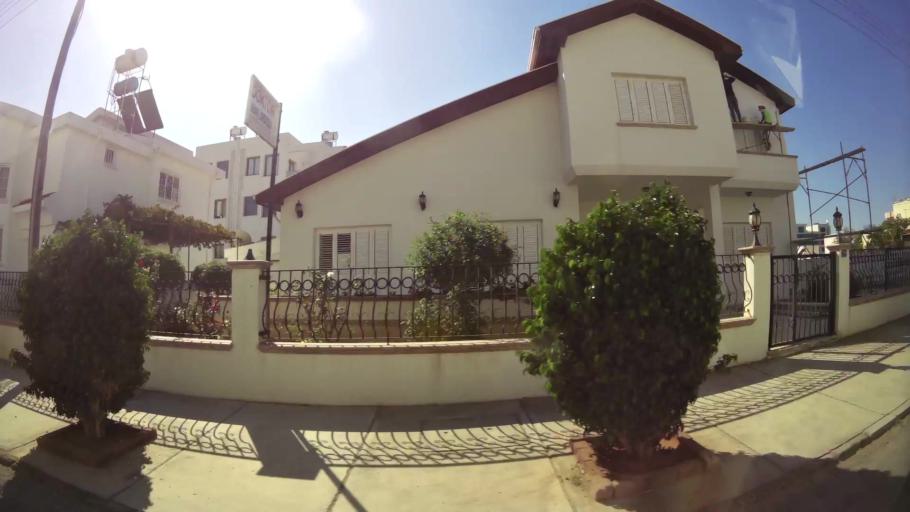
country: CY
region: Lefkosia
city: Nicosia
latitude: 35.2088
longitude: 33.3334
